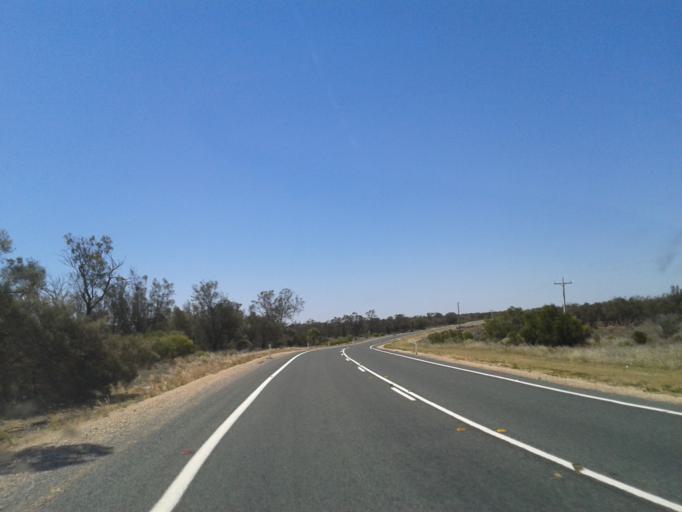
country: AU
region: New South Wales
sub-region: Wentworth
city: Dareton
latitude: -34.0983
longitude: 142.0909
